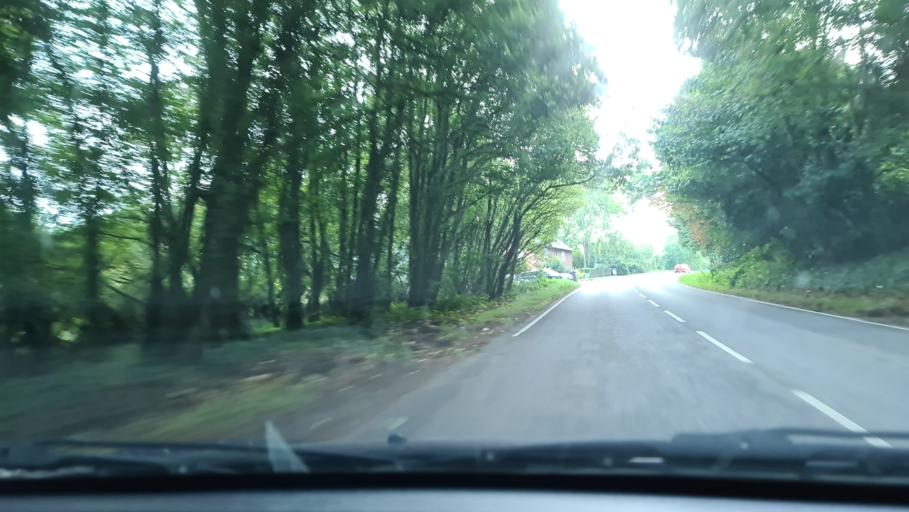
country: GB
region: England
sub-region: Hampshire
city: Romsey
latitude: 51.0137
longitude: -1.4957
